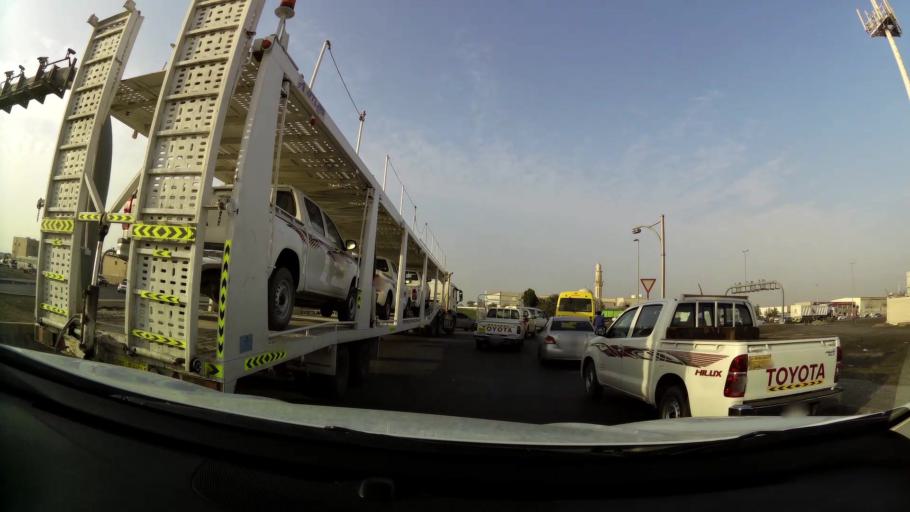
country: AE
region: Abu Dhabi
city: Abu Dhabi
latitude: 24.3588
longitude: 54.5019
